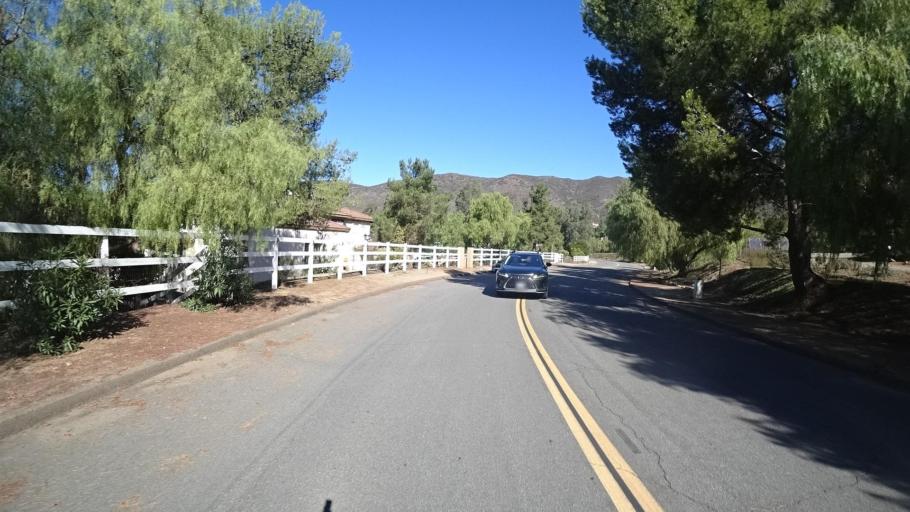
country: US
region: California
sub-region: San Diego County
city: Jamul
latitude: 32.7397
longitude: -116.8550
